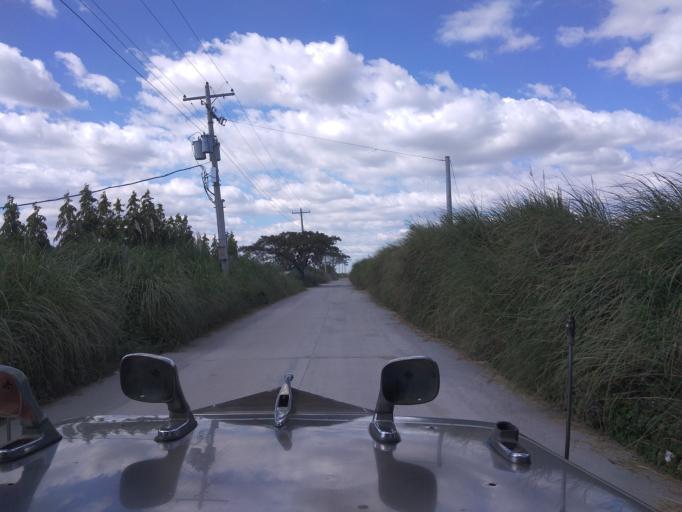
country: PH
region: Central Luzon
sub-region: Province of Pampanga
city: Magliman
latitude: 15.0456
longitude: 120.6281
